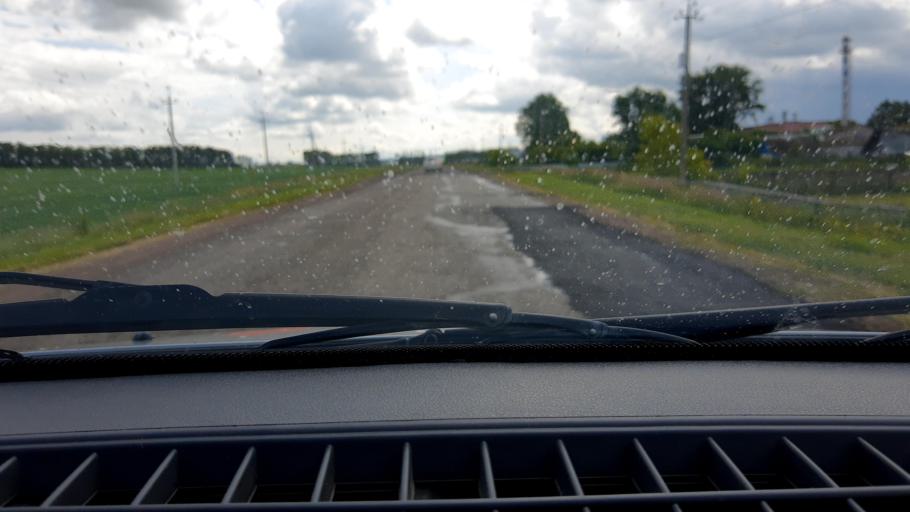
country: RU
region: Bashkortostan
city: Karmaskaly
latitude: 54.3968
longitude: 56.2455
